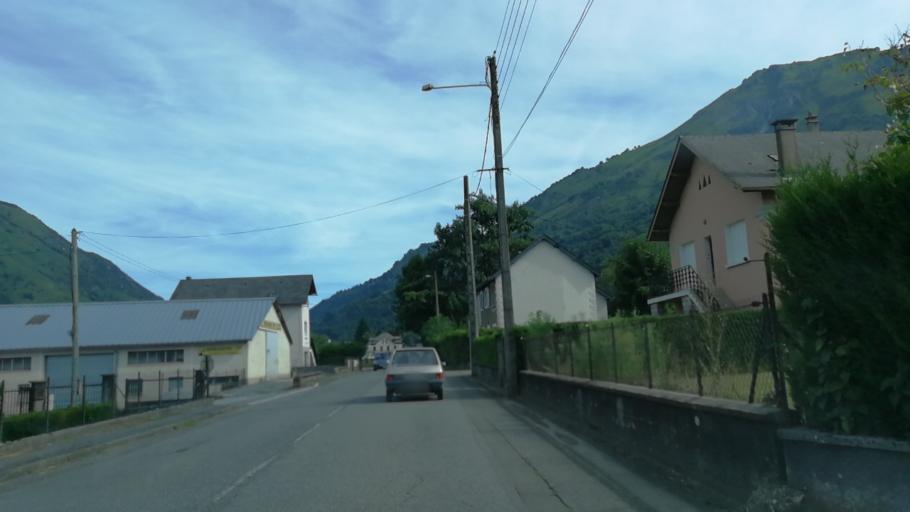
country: FR
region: Aquitaine
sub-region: Departement des Pyrenees-Atlantiques
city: Arette
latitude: 42.9925
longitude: -0.6026
